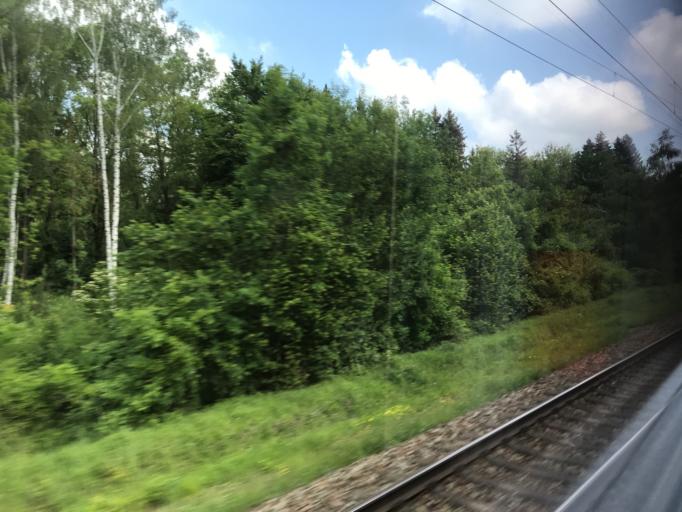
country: DE
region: Bavaria
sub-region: Swabia
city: Rettenbach
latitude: 48.4725
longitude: 10.3212
